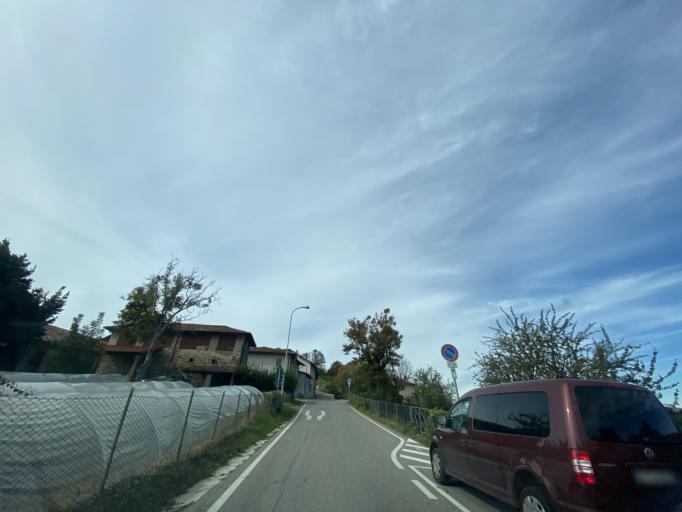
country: IT
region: Lombardy
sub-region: Provincia di Lecco
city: Montevecchia
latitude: 45.7080
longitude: 9.3700
